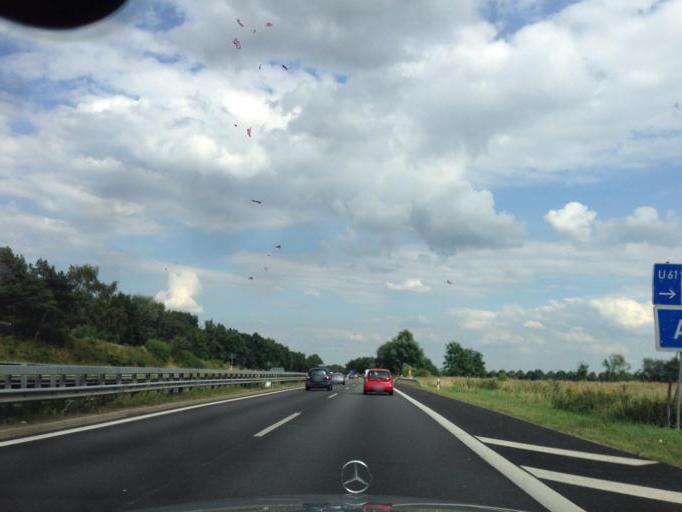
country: DE
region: Hamburg
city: Bergedorf
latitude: 53.4736
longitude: 10.1775
